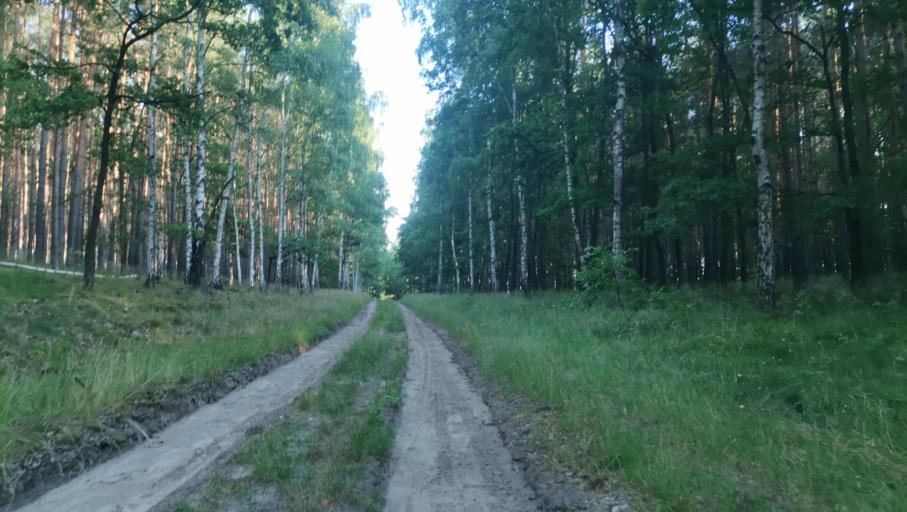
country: PL
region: Greater Poland Voivodeship
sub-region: Powiat jarocinski
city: Witaszyce
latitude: 51.9805
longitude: 17.5452
